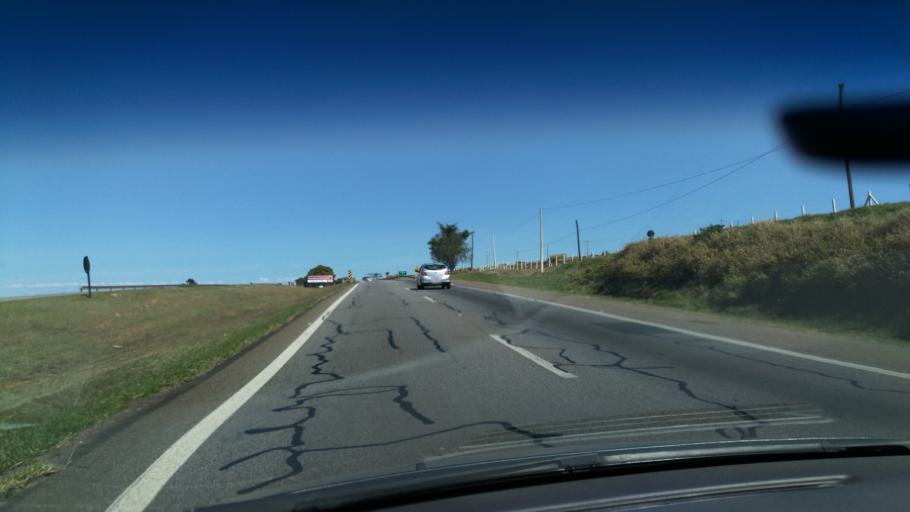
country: BR
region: Sao Paulo
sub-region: Santo Antonio De Posse
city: Santo Antonio de Posse
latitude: -22.5448
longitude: -46.9983
